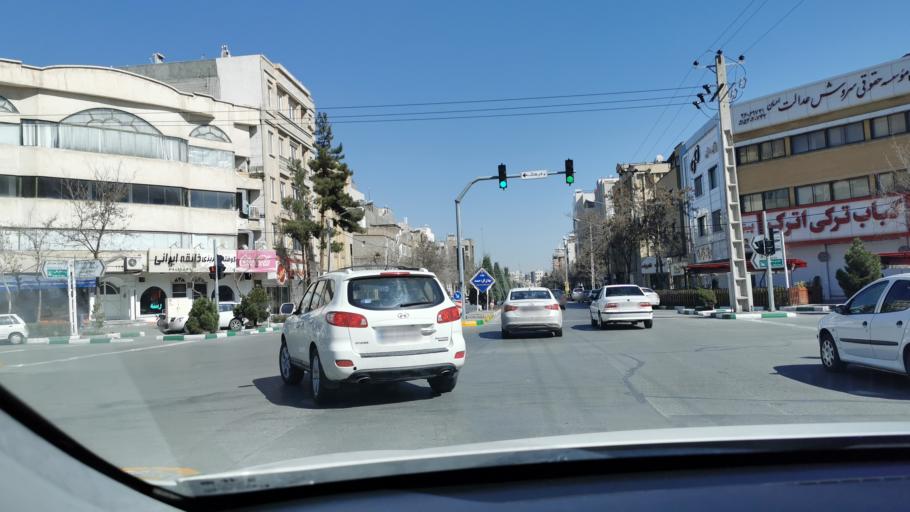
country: IR
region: Razavi Khorasan
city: Mashhad
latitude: 36.3242
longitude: 59.5266
